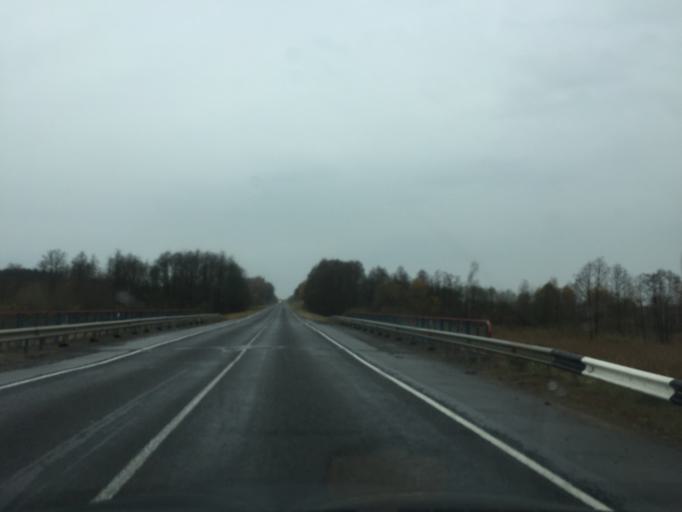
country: BY
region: Gomel
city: Karma
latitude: 53.3134
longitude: 30.7480
